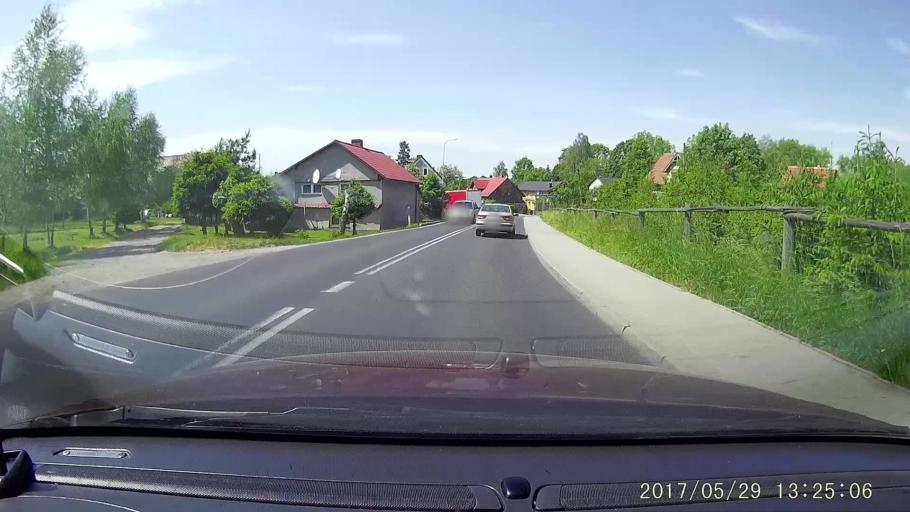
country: PL
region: Lower Silesian Voivodeship
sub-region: Powiat lubanski
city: Olszyna
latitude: 51.0391
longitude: 15.3854
